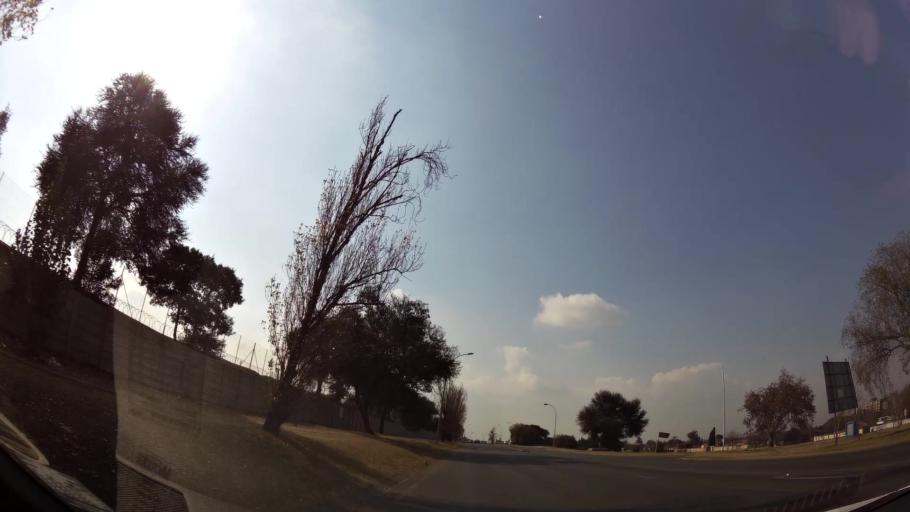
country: ZA
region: Gauteng
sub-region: Ekurhuleni Metropolitan Municipality
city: Germiston
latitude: -26.1780
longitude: 28.1911
